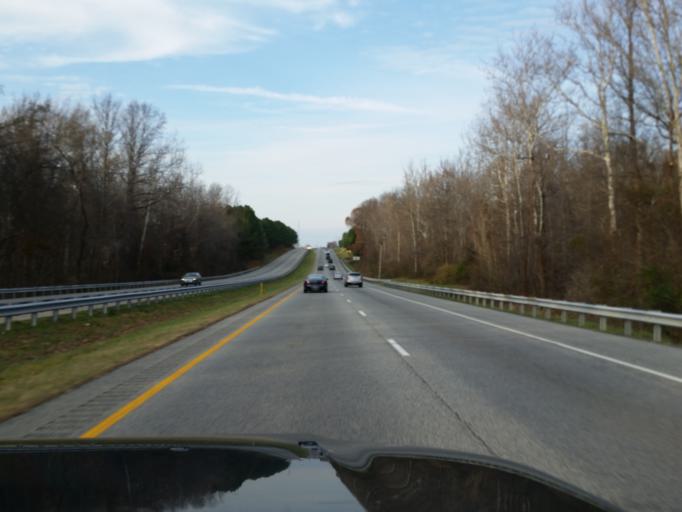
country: US
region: Maryland
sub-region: Queen Anne's County
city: Centreville
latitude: 38.9139
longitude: -76.0619
